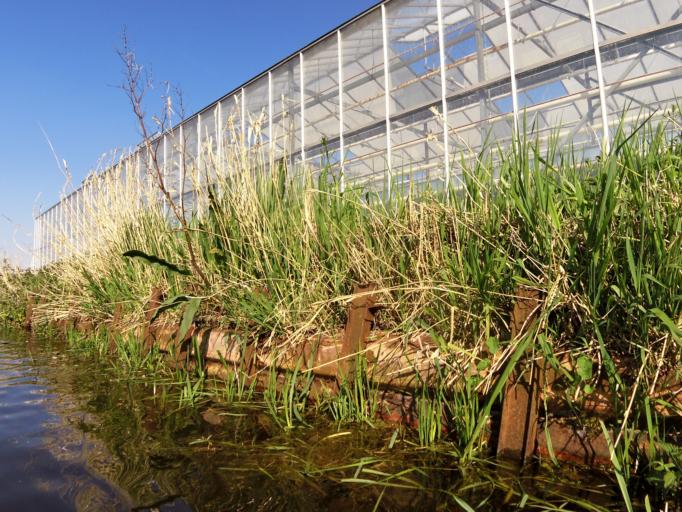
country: NL
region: South Holland
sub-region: Gemeente Voorschoten
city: Voorschoten
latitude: 52.1049
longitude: 4.4175
